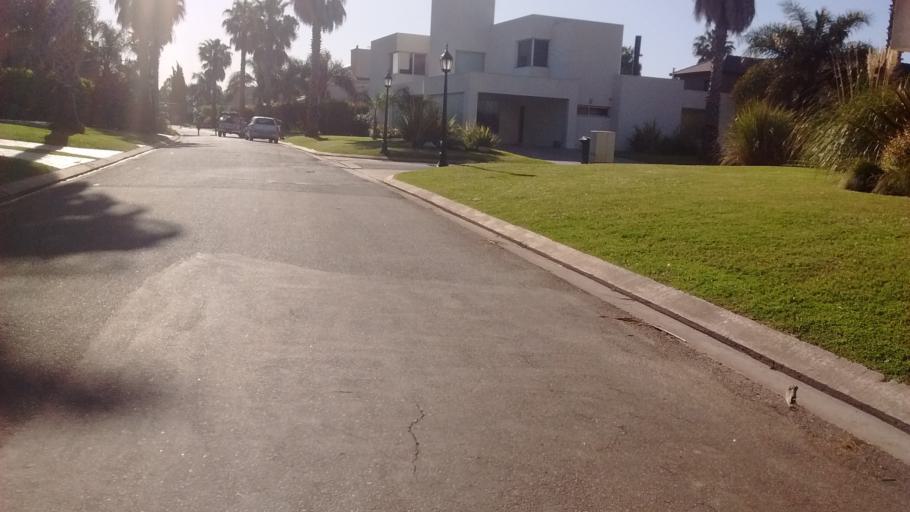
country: AR
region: Santa Fe
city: Funes
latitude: -32.9258
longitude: -60.8254
